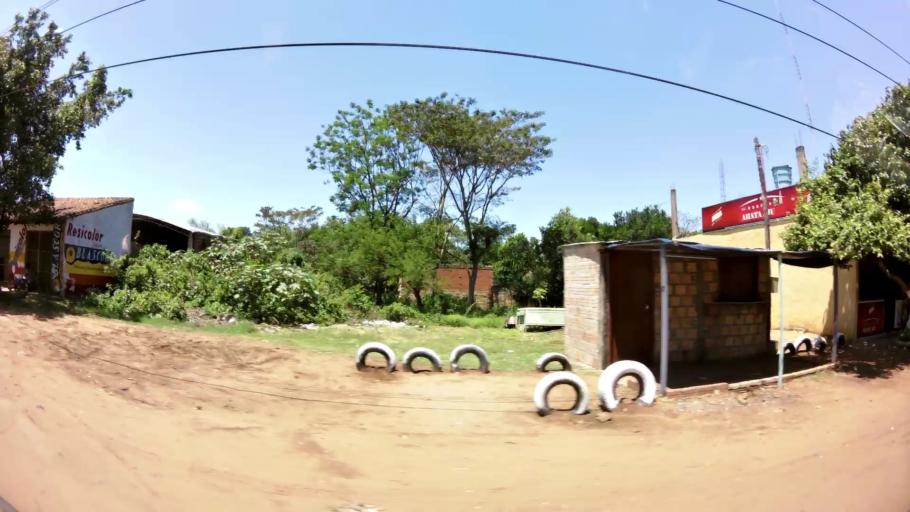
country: PY
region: Central
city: San Antonio
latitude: -25.4109
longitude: -57.5485
